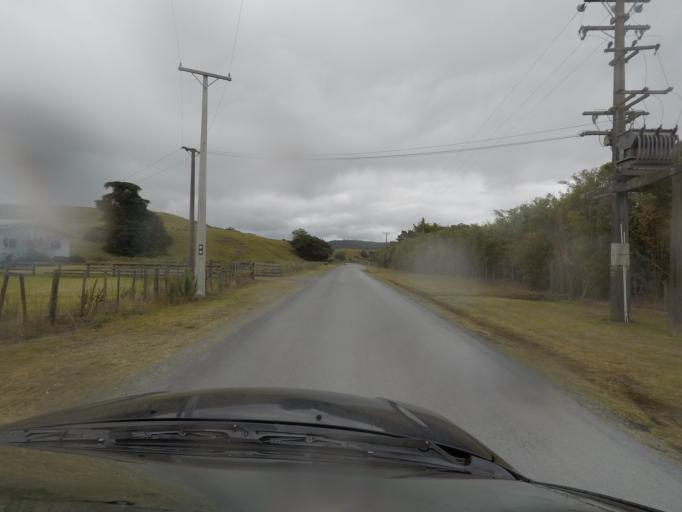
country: NZ
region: Auckland
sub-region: Auckland
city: Warkworth
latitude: -36.2458
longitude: 174.7228
